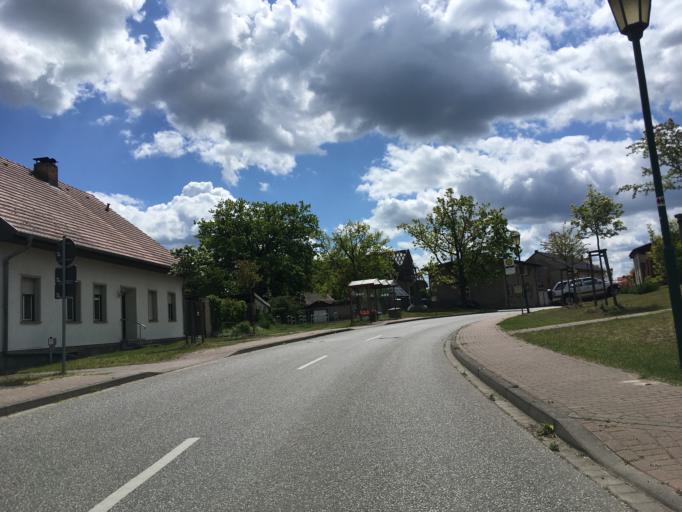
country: DE
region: Brandenburg
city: Liebenwalde
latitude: 52.8827
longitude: 13.4399
